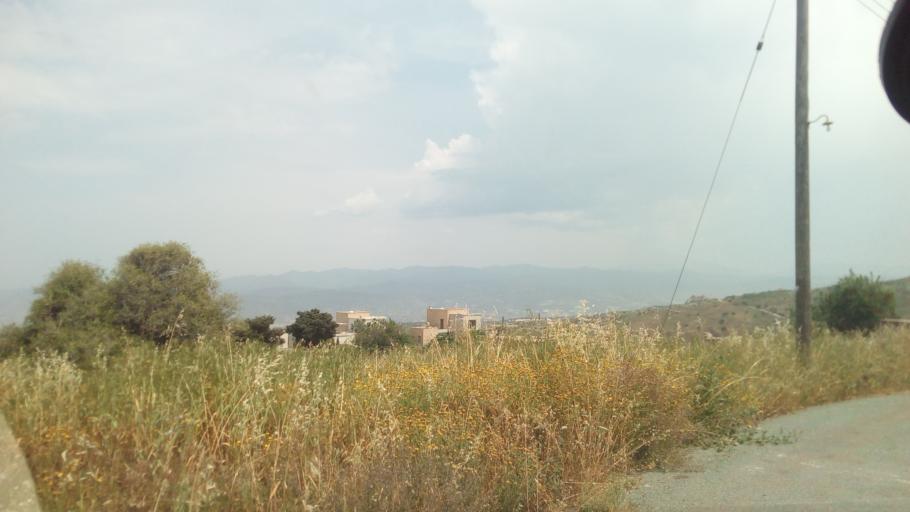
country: CY
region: Pafos
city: Polis
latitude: 34.9755
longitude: 32.3748
